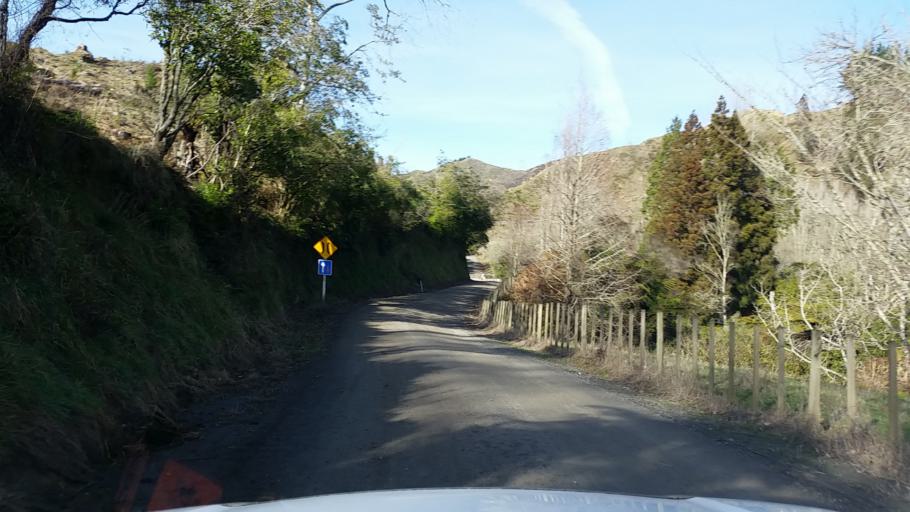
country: NZ
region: Taranaki
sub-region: South Taranaki District
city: Eltham
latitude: -39.3576
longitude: 174.5119
